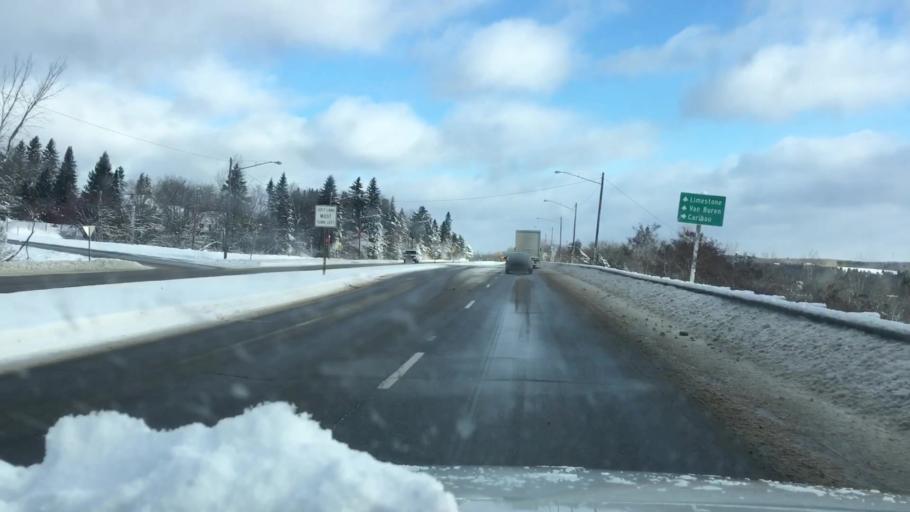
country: US
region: Maine
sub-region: Aroostook County
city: Caribou
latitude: 46.8606
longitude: -68.0032
